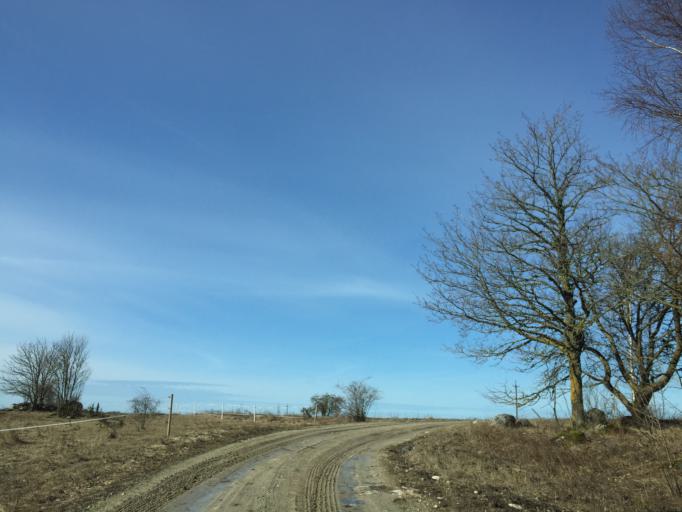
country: EE
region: Laeaene
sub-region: Haapsalu linn
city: Haapsalu
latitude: 58.6730
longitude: 23.5436
